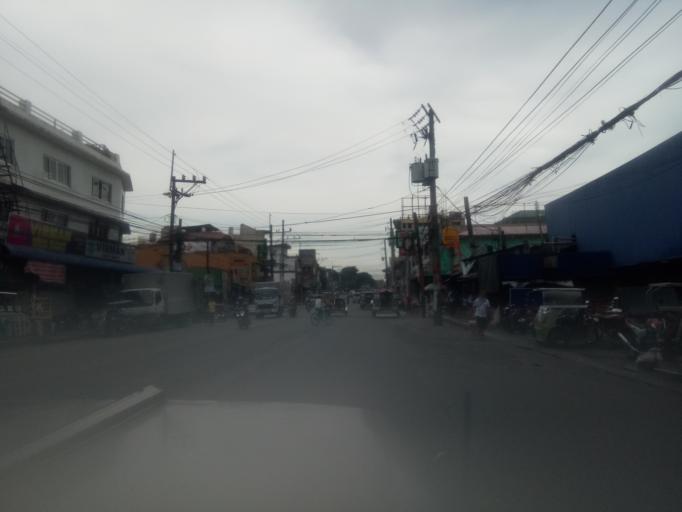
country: PH
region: Calabarzon
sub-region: Province of Cavite
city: Bulihan
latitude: 14.2937
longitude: 121.0061
